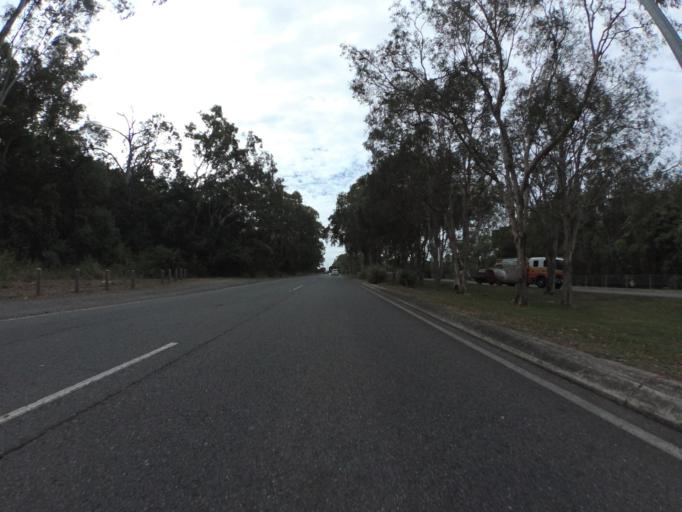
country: AU
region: Queensland
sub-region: Brisbane
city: Wynnum West
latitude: -27.4698
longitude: 153.1354
